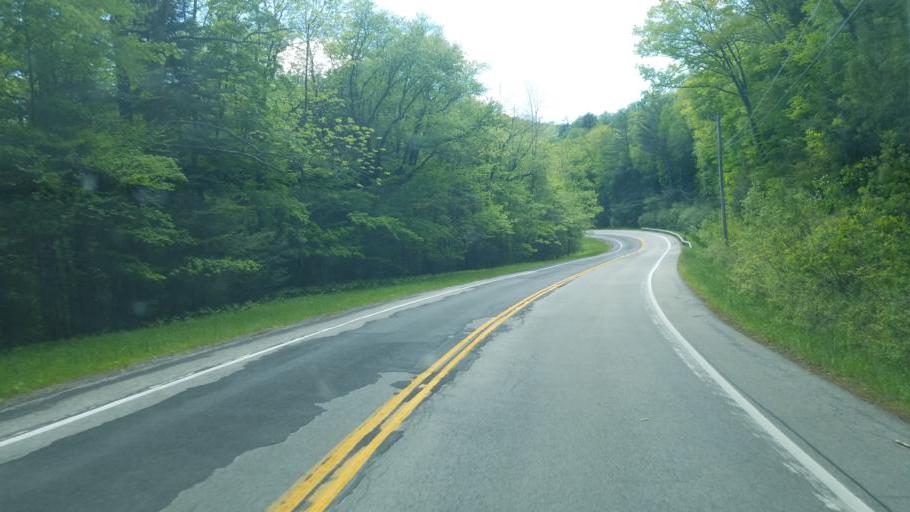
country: US
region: New York
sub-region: Fulton County
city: Gloversville
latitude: 43.2212
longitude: -74.5275
